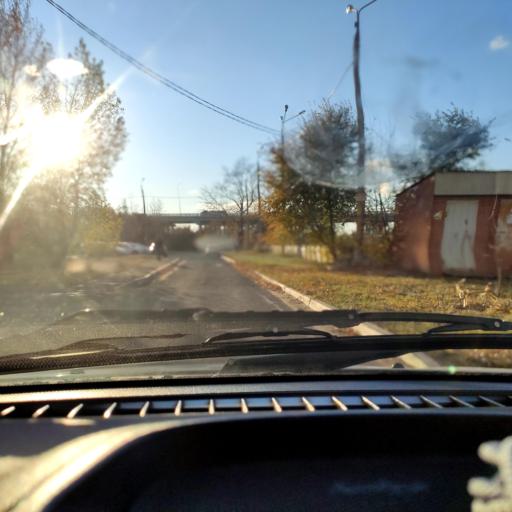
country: RU
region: Samara
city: Zhigulevsk
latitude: 53.4838
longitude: 49.5180
